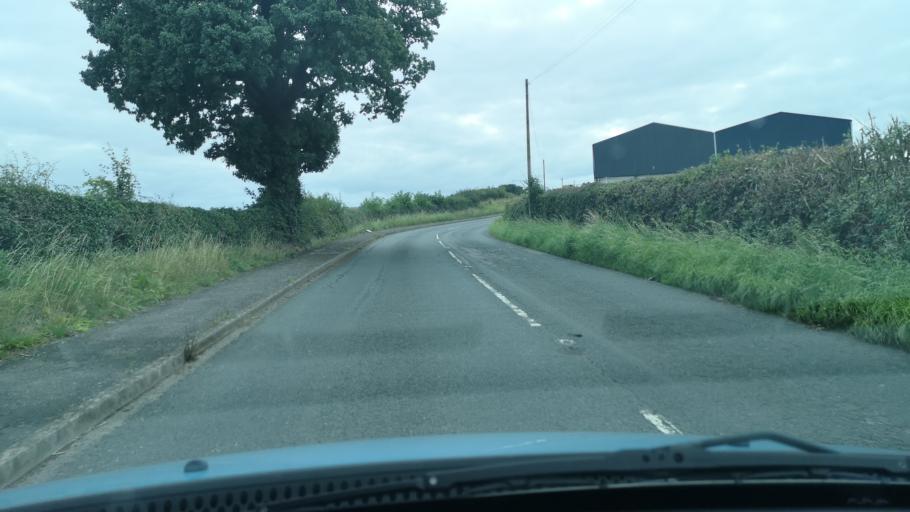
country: GB
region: England
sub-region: City and Borough of Wakefield
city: Crigglestone
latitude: 53.6333
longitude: -1.5465
